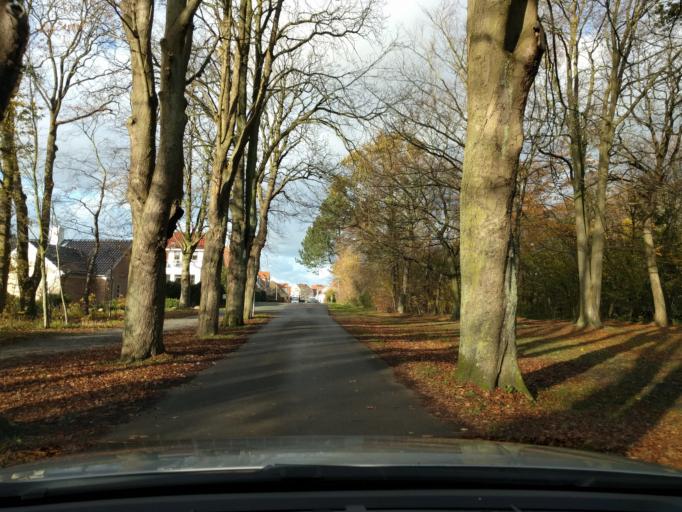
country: DK
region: South Denmark
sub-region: Kerteminde Kommune
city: Kerteminde
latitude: 55.4450
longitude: 10.6620
